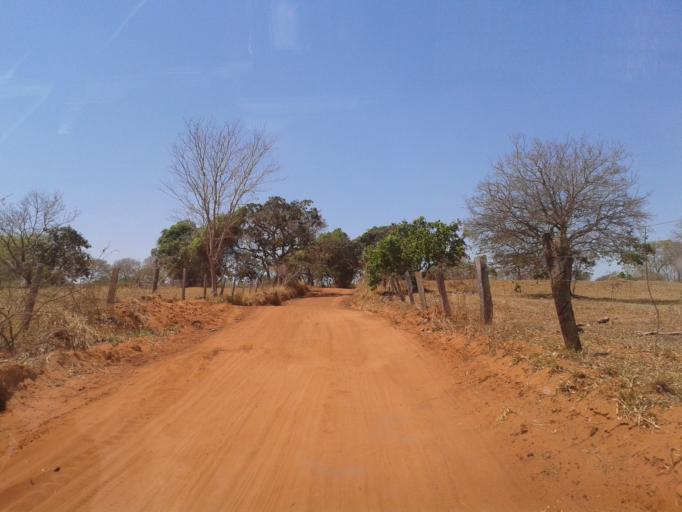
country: BR
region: Minas Gerais
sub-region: Ituiutaba
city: Ituiutaba
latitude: -19.0808
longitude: -49.3094
